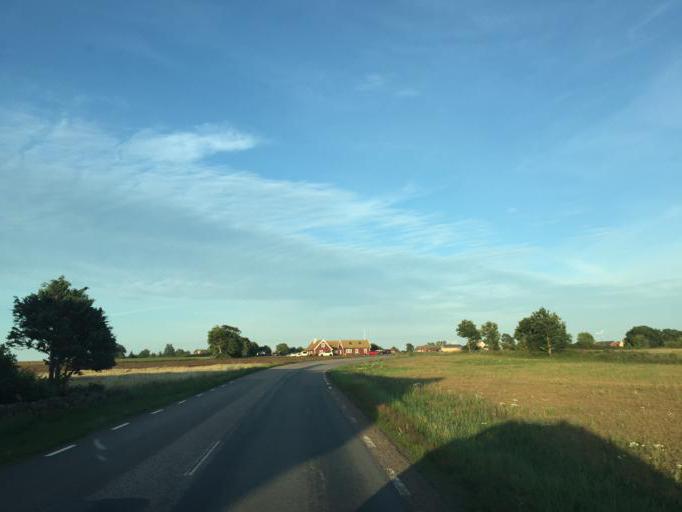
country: SE
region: Skane
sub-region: Angelholms Kommun
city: Vejbystrand
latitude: 56.3177
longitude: 12.7811
